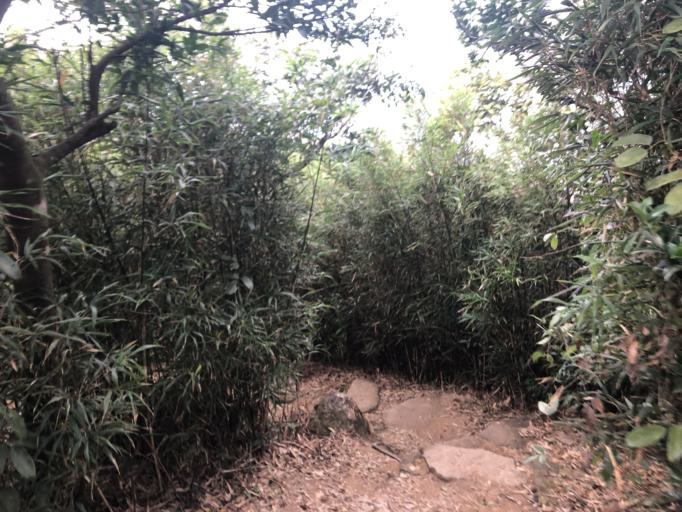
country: HK
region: Wanchai
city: Wan Chai
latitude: 22.2678
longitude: 114.2110
